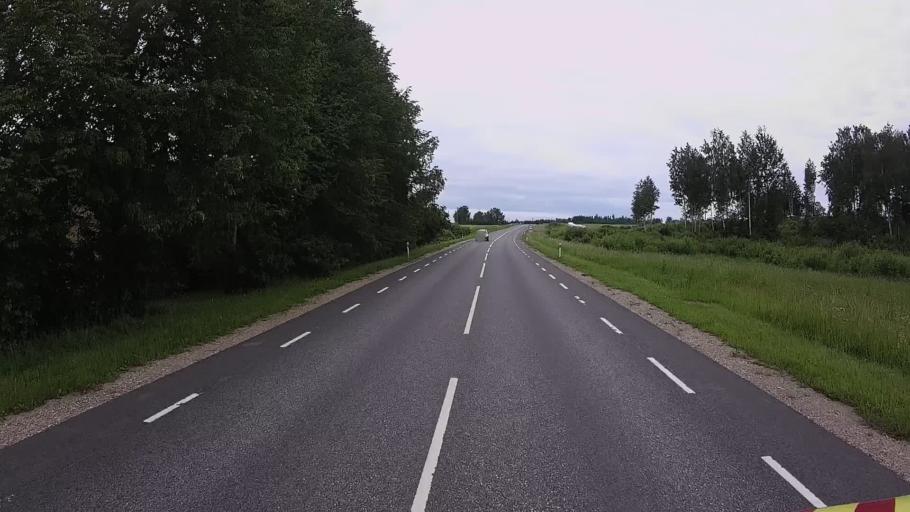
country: EE
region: Viljandimaa
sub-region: Karksi vald
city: Karksi-Nuia
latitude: 58.1468
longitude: 25.5925
